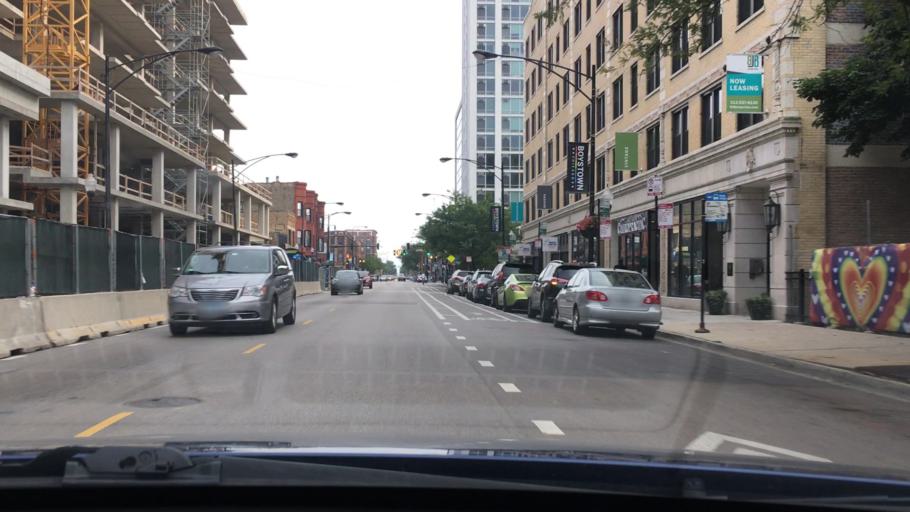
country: US
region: Illinois
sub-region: Cook County
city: Lincolnwood
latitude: 41.9526
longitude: -87.6497
